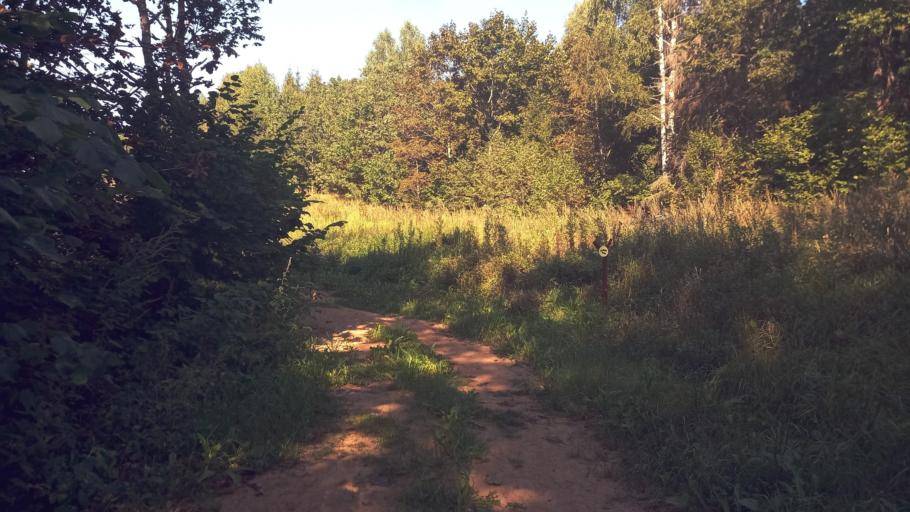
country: LT
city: Varniai
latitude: 55.8798
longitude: 22.3515
